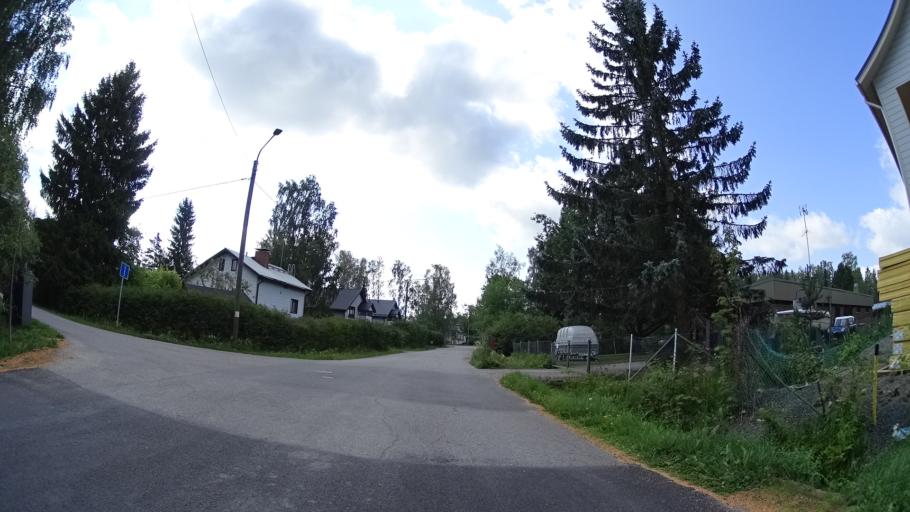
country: FI
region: Uusimaa
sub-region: Helsinki
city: Helsinki
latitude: 60.2805
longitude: 24.9161
